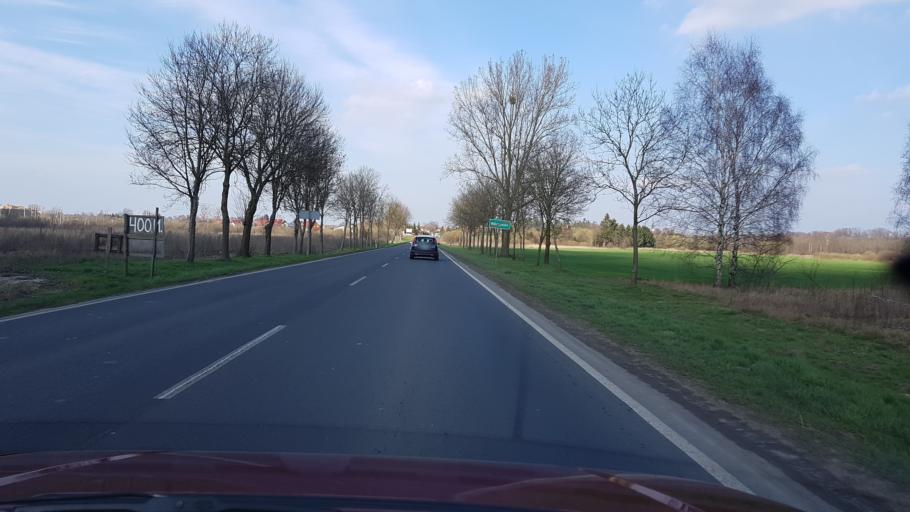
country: PL
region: West Pomeranian Voivodeship
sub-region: Powiat gryficki
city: Ploty
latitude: 53.7920
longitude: 15.2544
